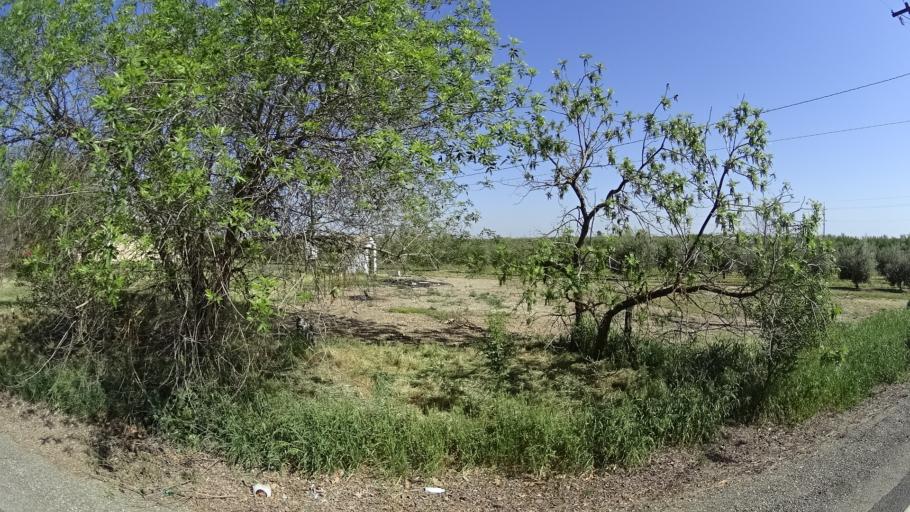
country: US
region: California
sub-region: Glenn County
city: Hamilton City
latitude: 39.6596
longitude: -122.0093
